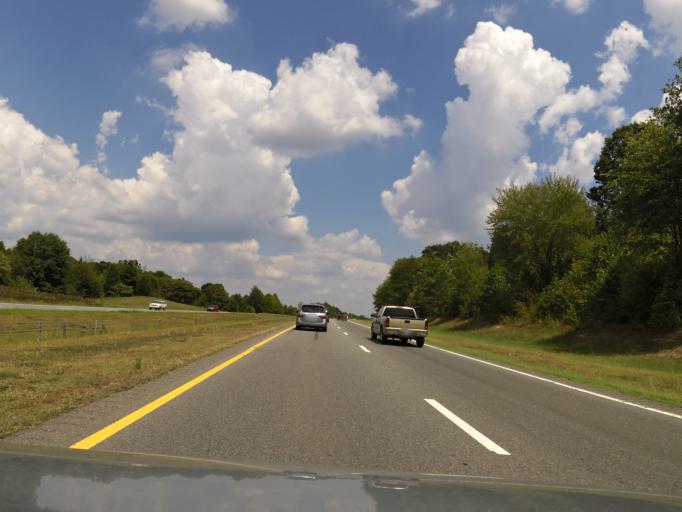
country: US
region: North Carolina
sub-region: Cleveland County
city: White Plains
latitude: 35.2531
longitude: -81.3970
